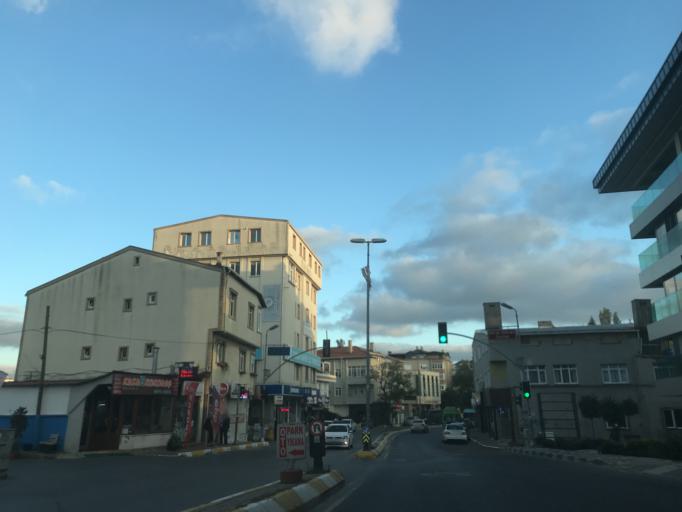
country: TR
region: Istanbul
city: Sisli
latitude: 41.1326
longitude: 29.0399
